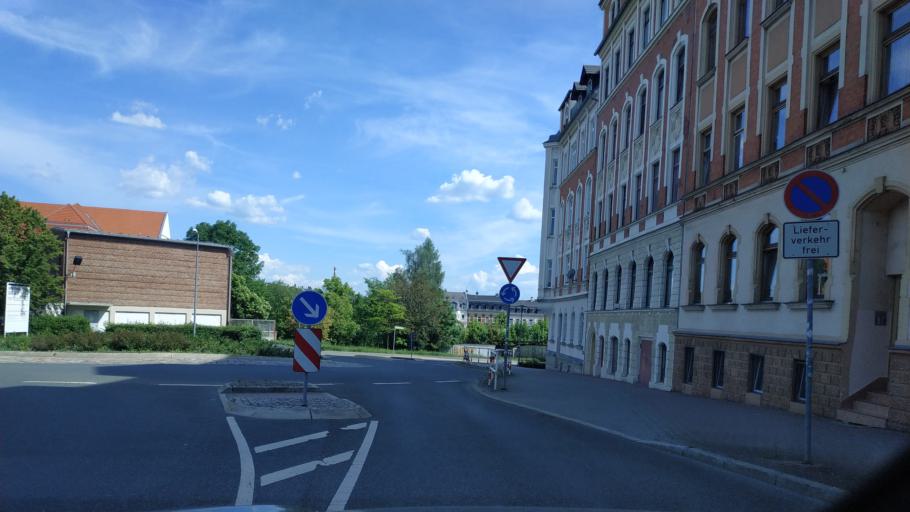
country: DE
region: Saxony
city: Plauen
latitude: 50.5087
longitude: 12.1362
